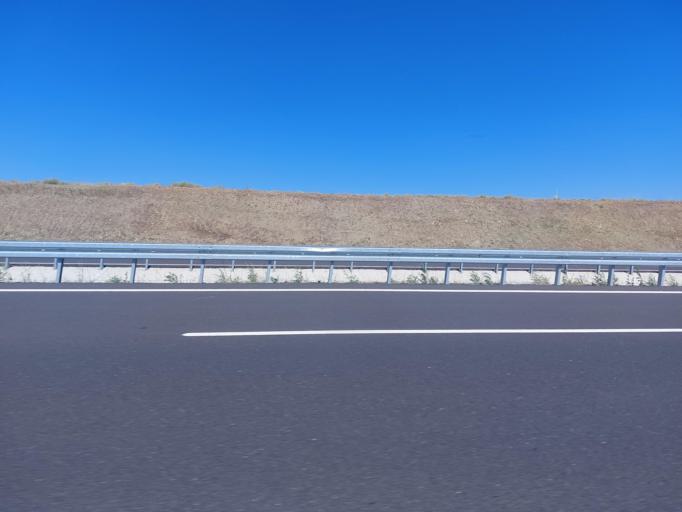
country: TR
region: Tekirdag
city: Balli
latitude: 40.7386
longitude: 26.9896
